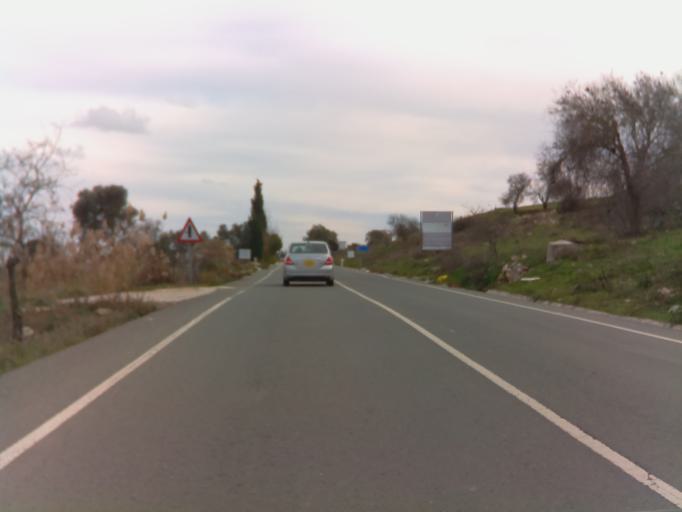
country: CY
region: Pafos
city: Polis
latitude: 34.9660
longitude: 32.4121
